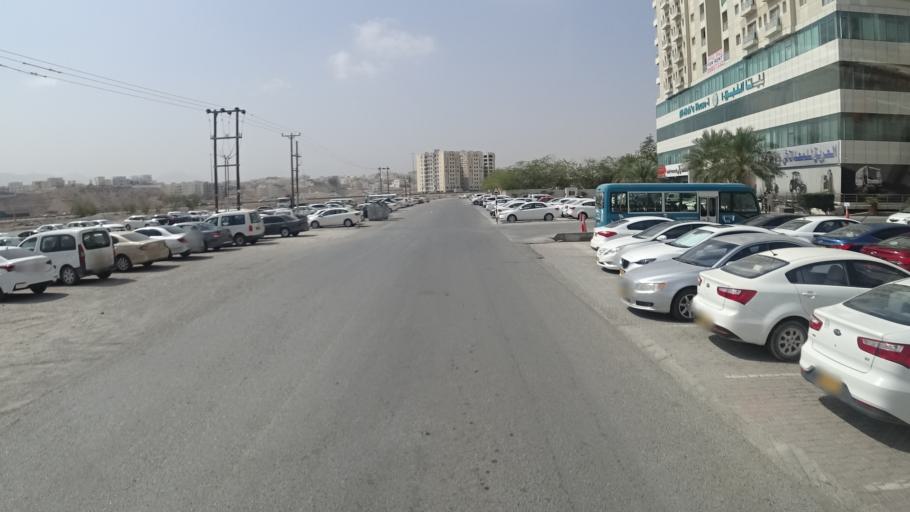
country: OM
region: Muhafazat Masqat
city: Bawshar
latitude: 23.5655
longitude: 58.3471
